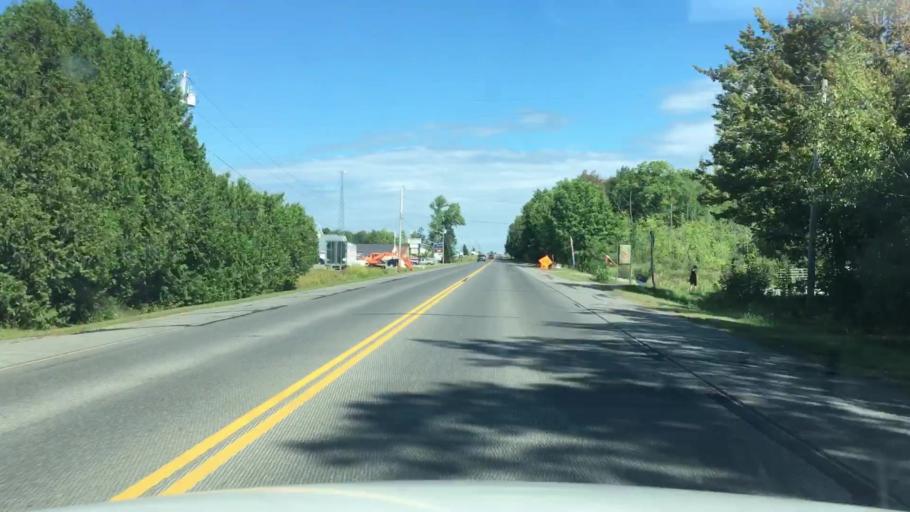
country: US
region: Maine
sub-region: Penobscot County
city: Newport
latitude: 44.8692
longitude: -69.2833
